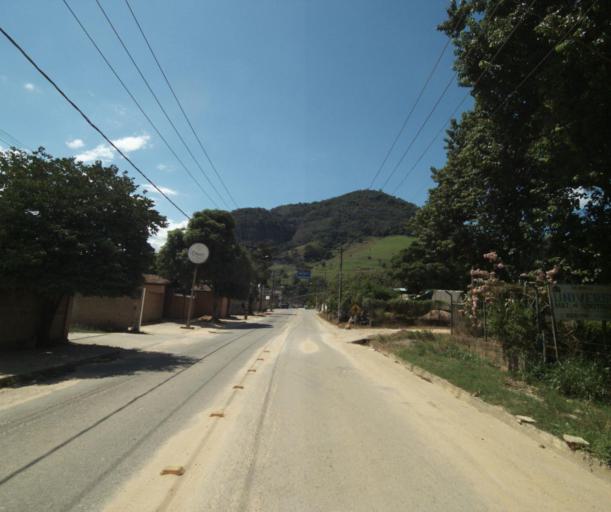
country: BR
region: Espirito Santo
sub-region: Mimoso Do Sul
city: Mimoso do Sul
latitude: -21.0768
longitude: -41.3553
